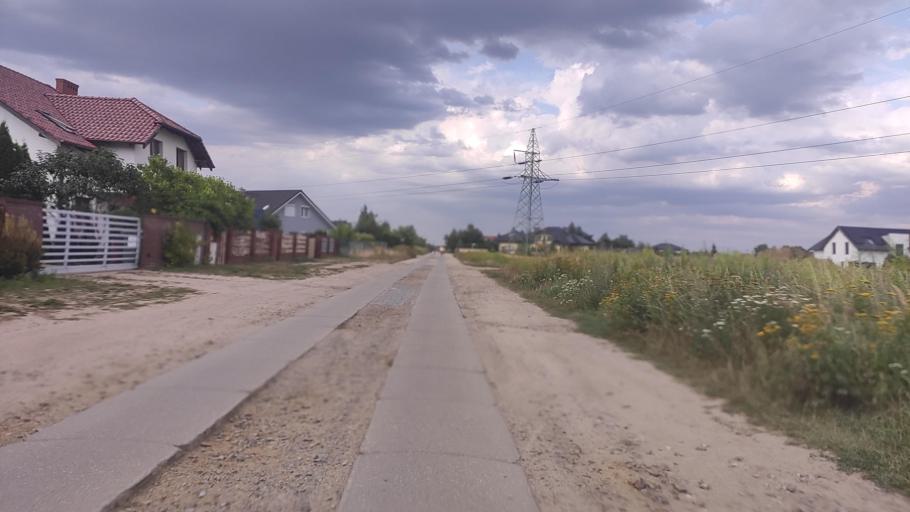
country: PL
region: Greater Poland Voivodeship
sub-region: Powiat poznanski
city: Swarzedz
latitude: 52.4113
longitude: 17.1005
